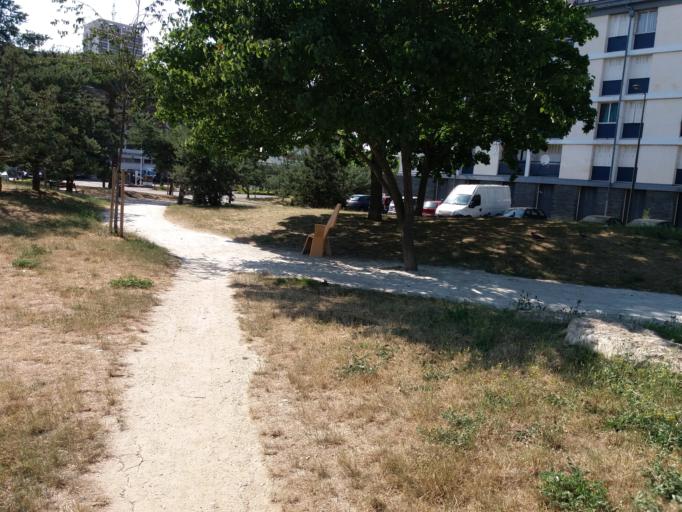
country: FR
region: Centre
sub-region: Departement d'Indre-et-Loire
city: Tours
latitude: 47.3802
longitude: 0.6994
